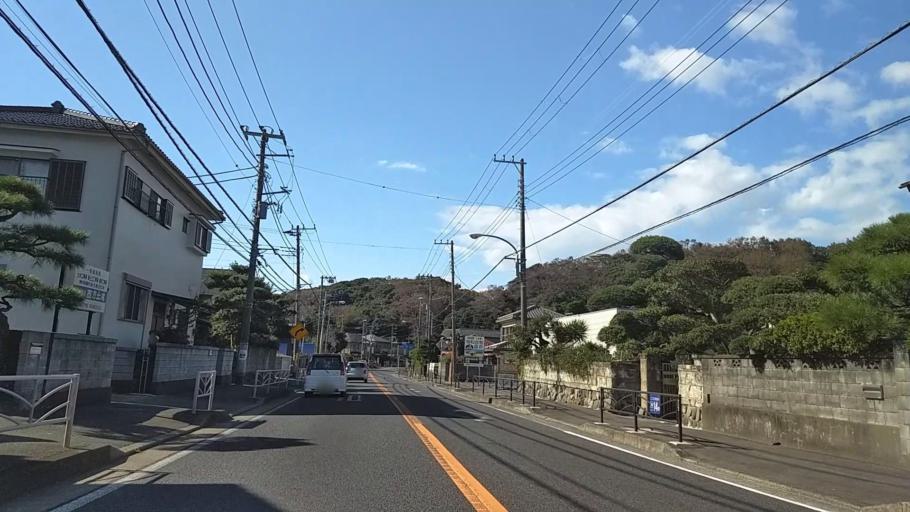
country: JP
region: Kanagawa
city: Oiso
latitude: 35.3045
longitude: 139.2929
